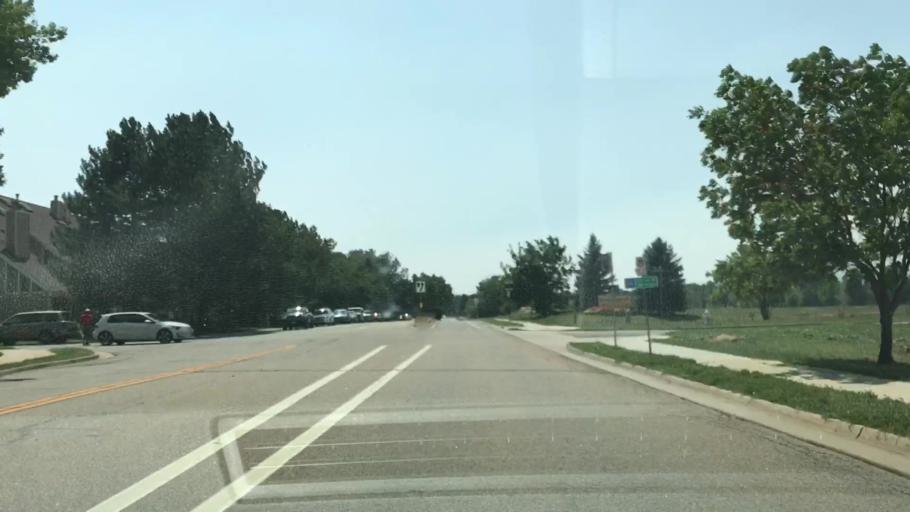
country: US
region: Colorado
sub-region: Boulder County
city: Gunbarrel
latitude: 40.0622
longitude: -105.2162
